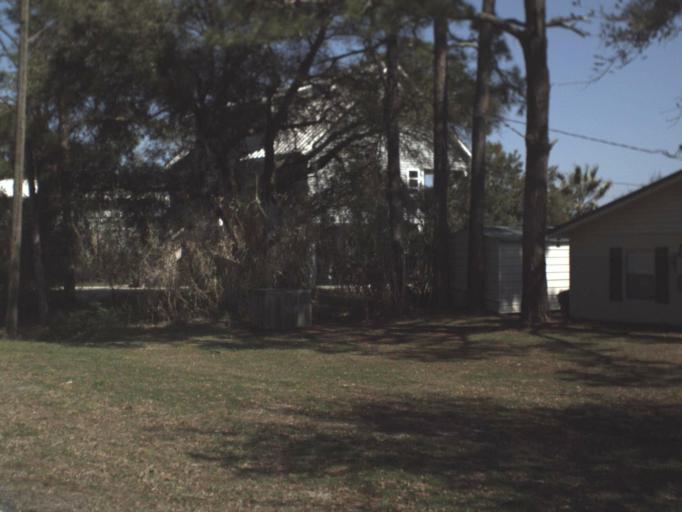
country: US
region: Florida
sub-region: Franklin County
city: Carrabelle
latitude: 29.8772
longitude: -84.6022
